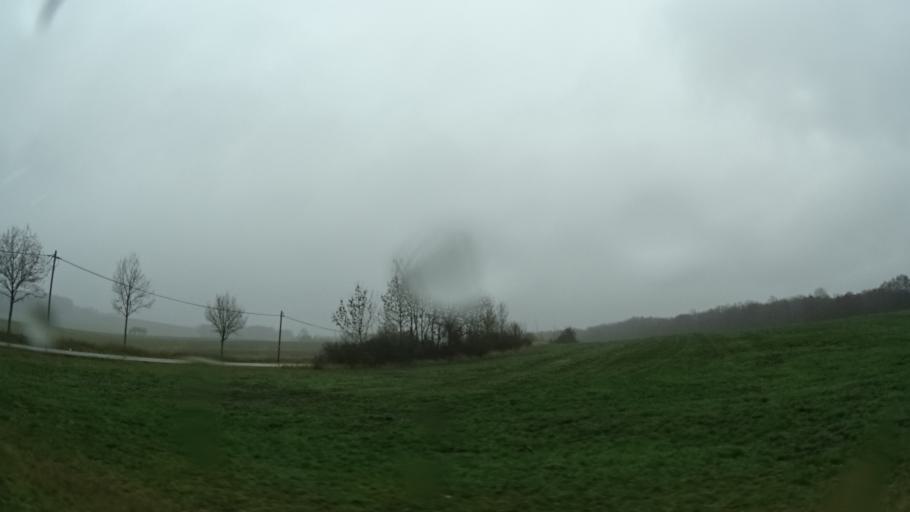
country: DE
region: Thuringia
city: Gleichamberg
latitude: 50.3964
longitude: 10.6319
